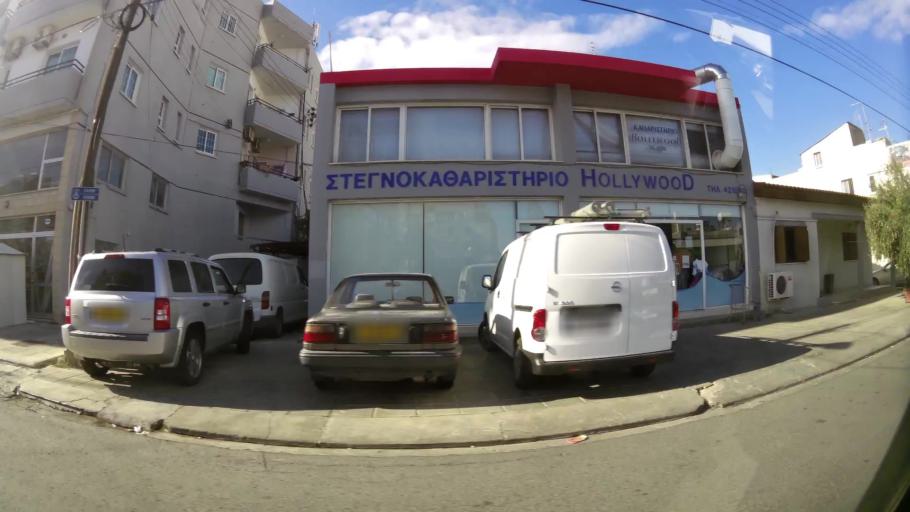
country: CY
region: Lefkosia
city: Nicosia
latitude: 35.1362
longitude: 33.3523
